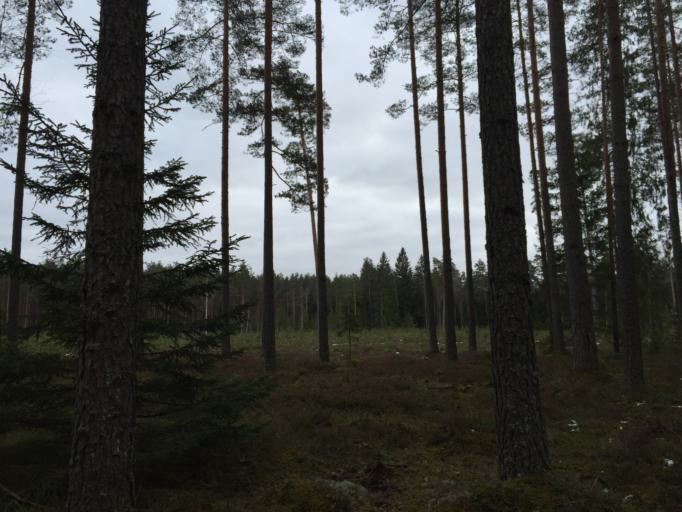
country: LV
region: Garkalne
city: Garkalne
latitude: 56.9651
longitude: 24.4748
